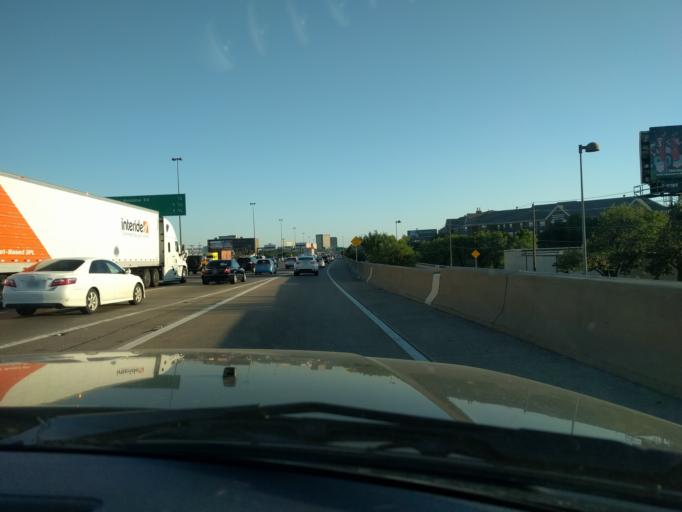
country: US
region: Texas
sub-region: Dallas County
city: Richardson
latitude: 32.9066
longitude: -96.7693
